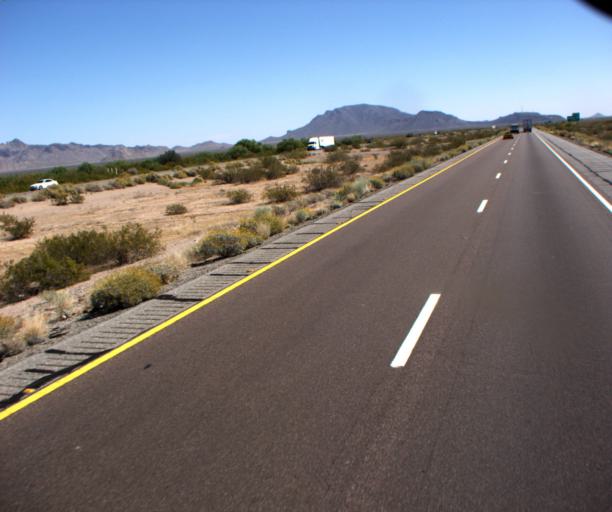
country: US
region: Arizona
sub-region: La Paz County
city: Salome
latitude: 33.5425
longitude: -113.1809
